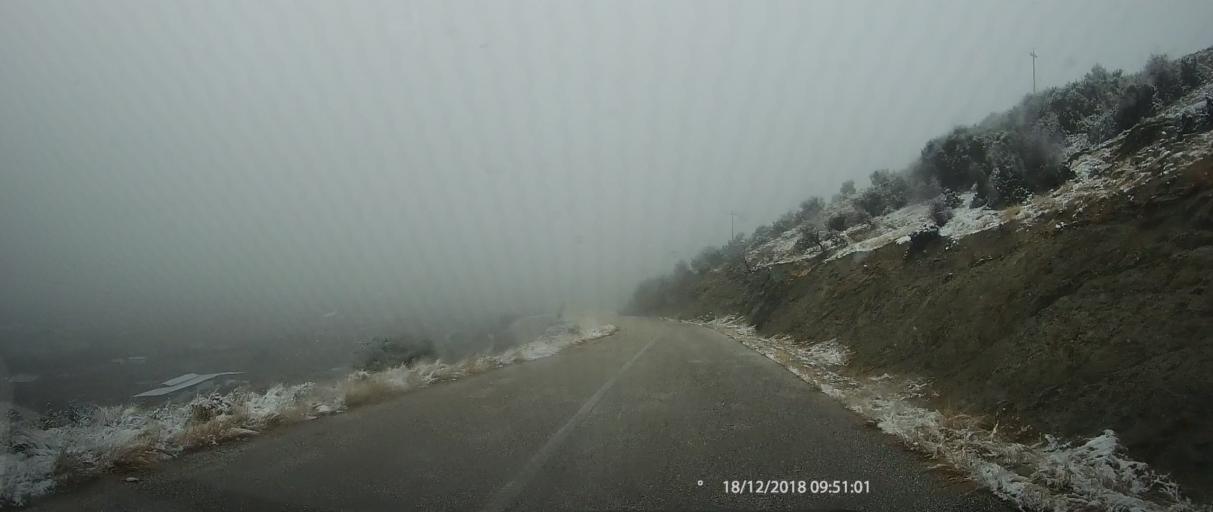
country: GR
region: Thessaly
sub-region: Nomos Larisis
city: Livadi
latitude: 40.0296
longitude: 22.2518
